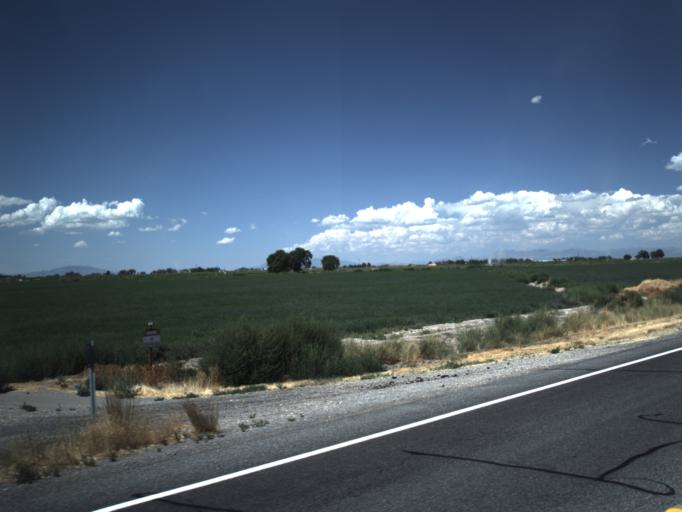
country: US
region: Utah
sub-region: Millard County
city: Delta
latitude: 39.3450
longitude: -112.6007
